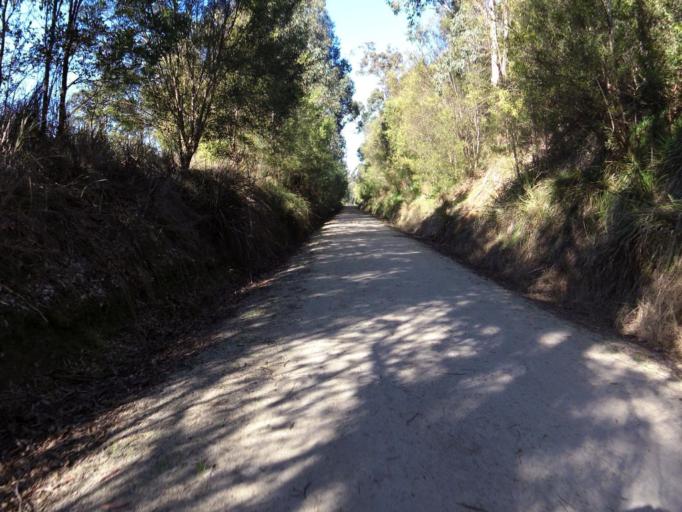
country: AU
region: Victoria
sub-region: Latrobe
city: Morwell
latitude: -38.3827
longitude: 146.2606
